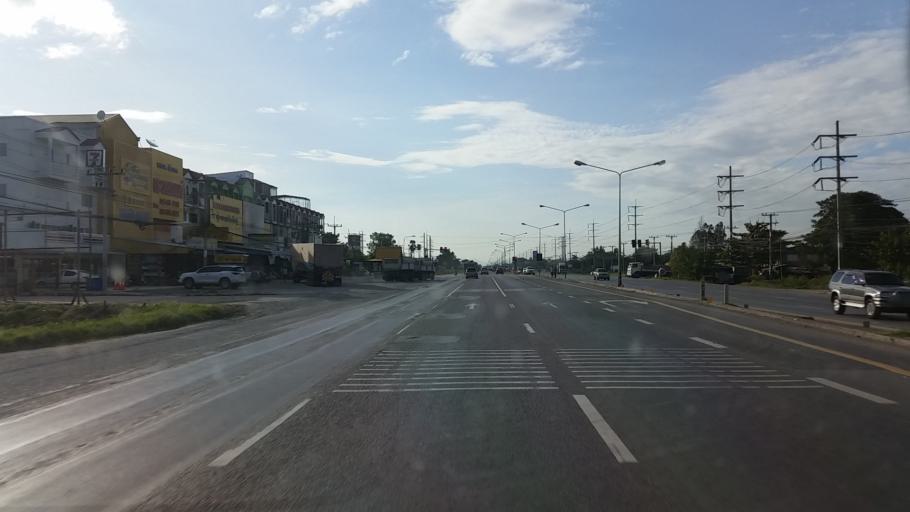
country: TH
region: Sara Buri
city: Chaloem Phra Kiat
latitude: 14.6065
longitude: 100.8947
